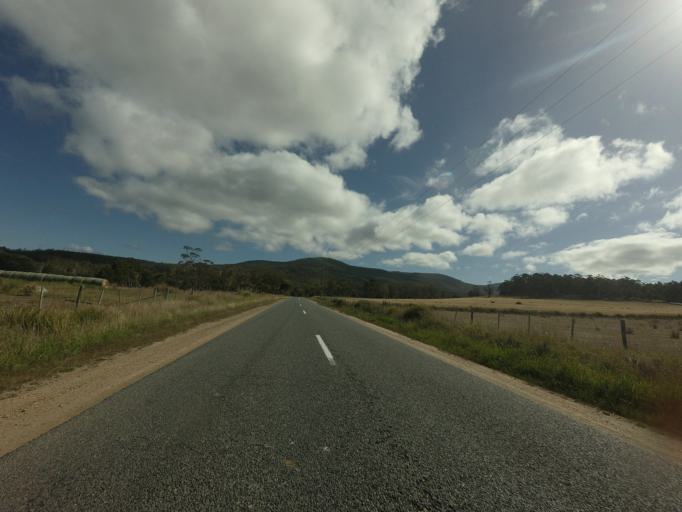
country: AU
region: Tasmania
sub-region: Break O'Day
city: St Helens
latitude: -41.7766
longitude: 148.2605
